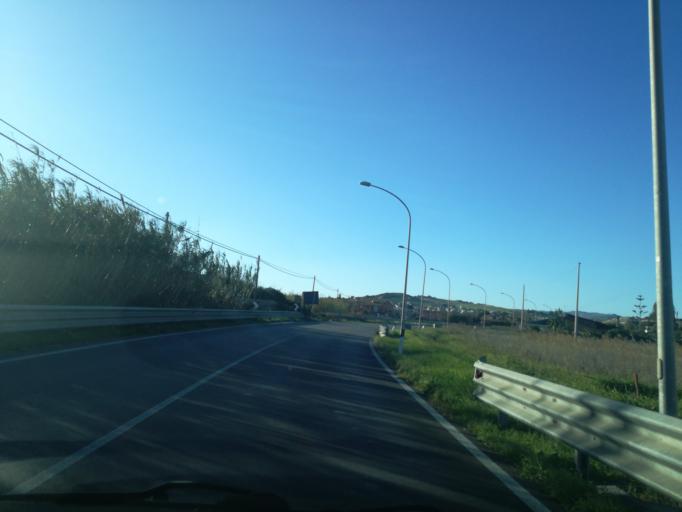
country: IT
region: Sicily
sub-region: Provincia di Caltanissetta
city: Gela
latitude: 37.0968
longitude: 14.1666
